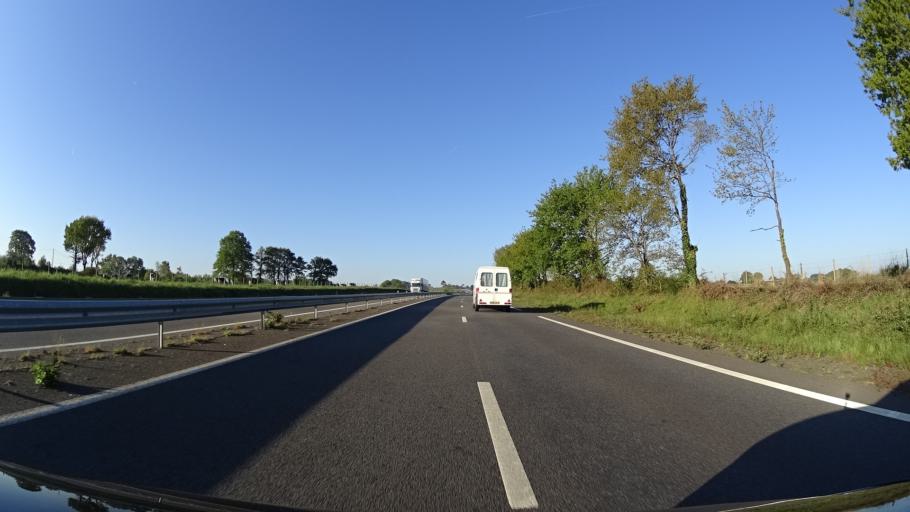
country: FR
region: Brittany
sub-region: Departement d'Ille-et-Vilaine
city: Pipriac
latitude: 47.8241
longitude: -1.9129
